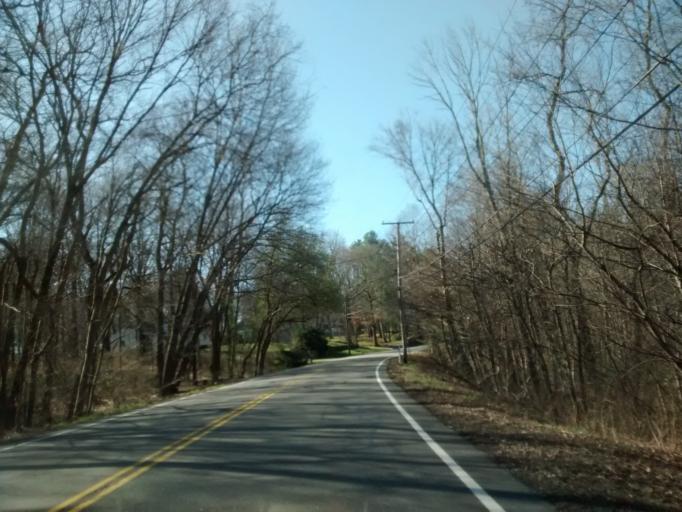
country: US
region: Massachusetts
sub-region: Worcester County
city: Westborough
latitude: 42.2495
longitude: -71.6019
